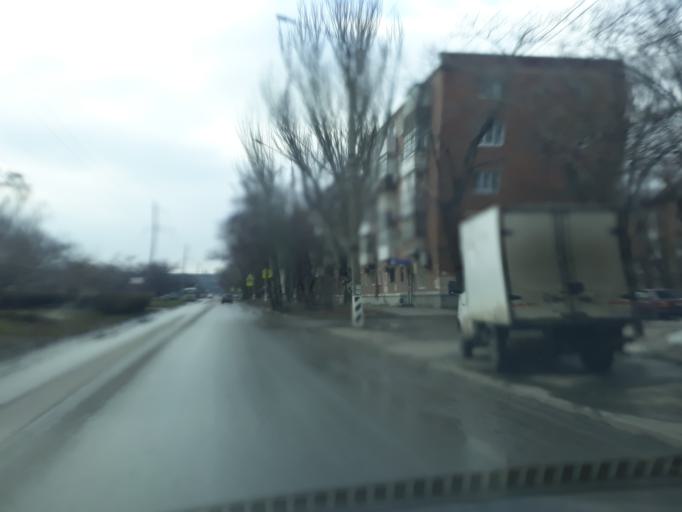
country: RU
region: Rostov
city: Taganrog
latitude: 47.2498
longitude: 38.9143
